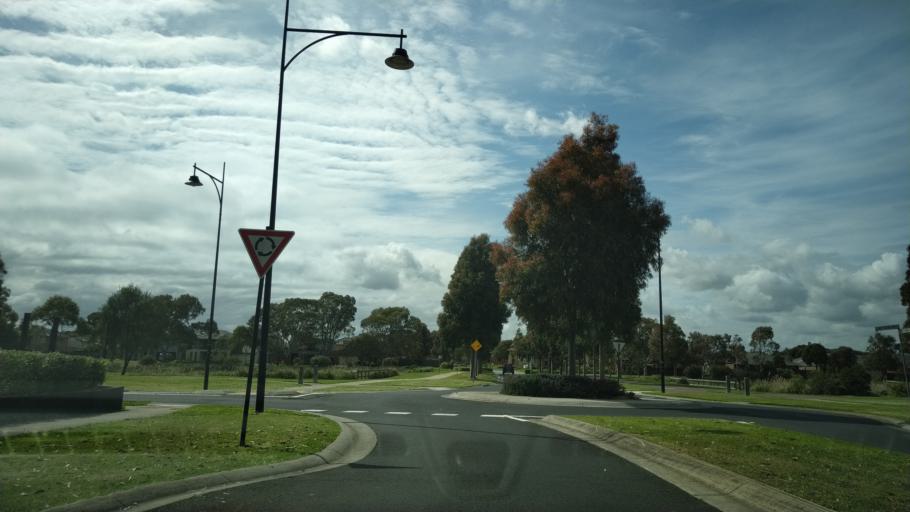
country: AU
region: Victoria
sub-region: Kingston
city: Waterways
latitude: -38.0043
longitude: 145.1495
